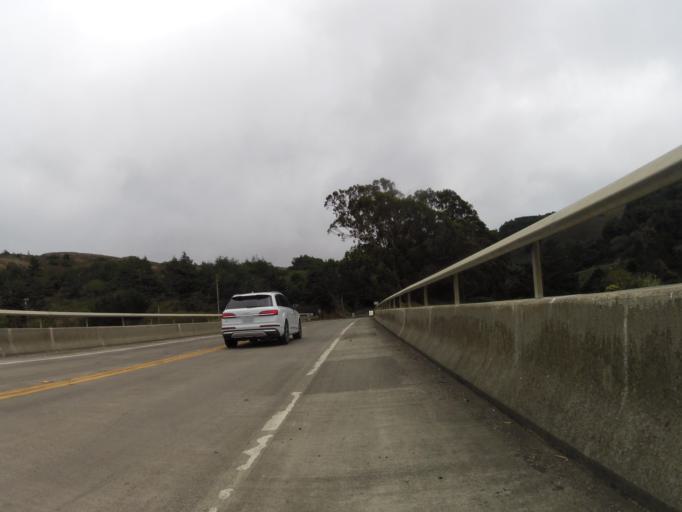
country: US
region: California
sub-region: Sonoma County
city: Monte Rio
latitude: 38.4347
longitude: -123.1011
